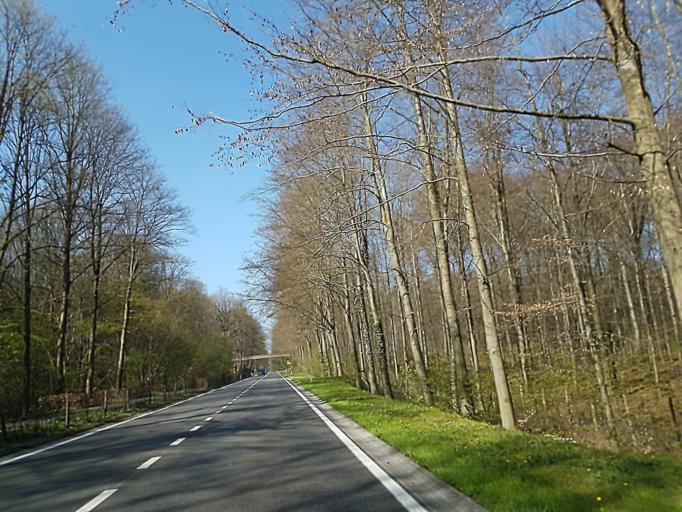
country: BE
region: Flanders
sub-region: Provincie Vlaams-Brabant
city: Oud-Heverlee
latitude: 50.8060
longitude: 4.7074
